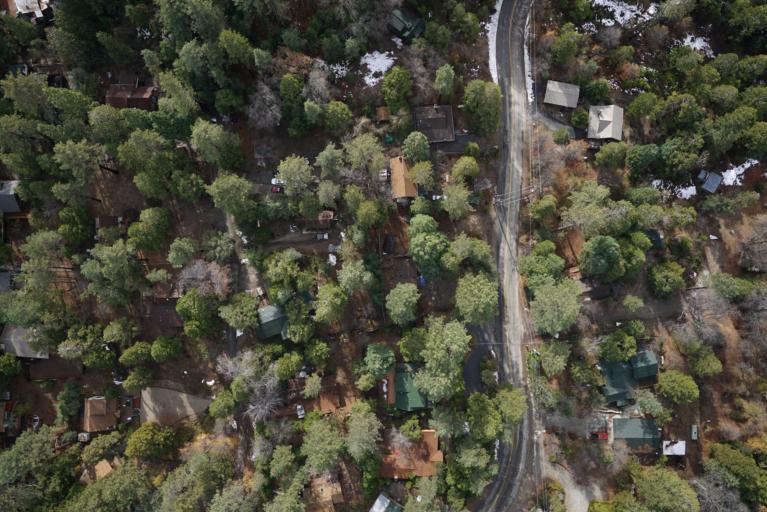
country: US
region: California
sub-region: Riverside County
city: Idyllwild
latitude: 33.7445
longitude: -116.7041
